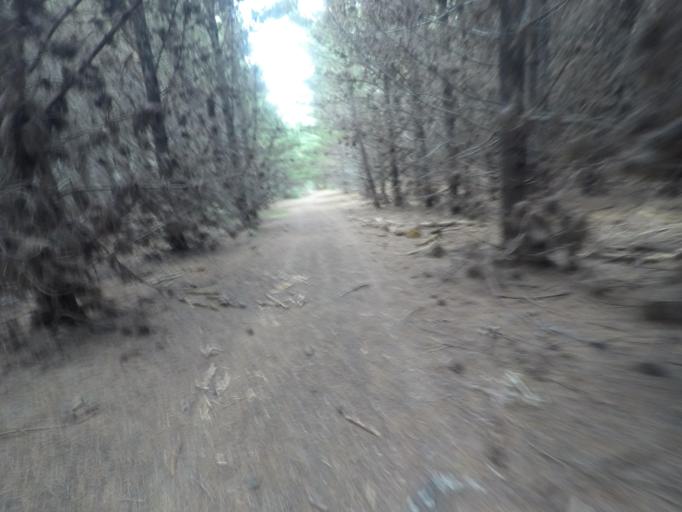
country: NZ
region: Auckland
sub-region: Auckland
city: Parakai
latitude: -36.6025
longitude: 174.2730
